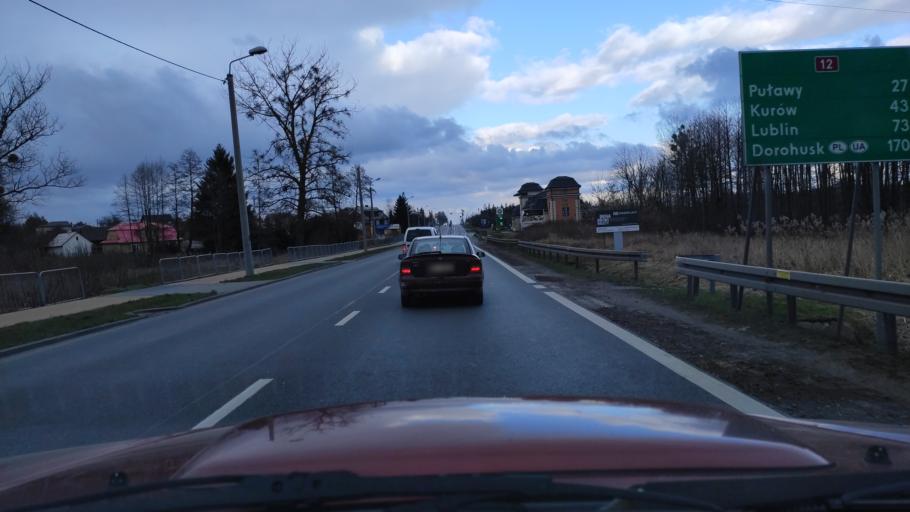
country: PL
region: Masovian Voivodeship
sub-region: Powiat zwolenski
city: Zwolen
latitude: 51.3558
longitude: 21.5915
